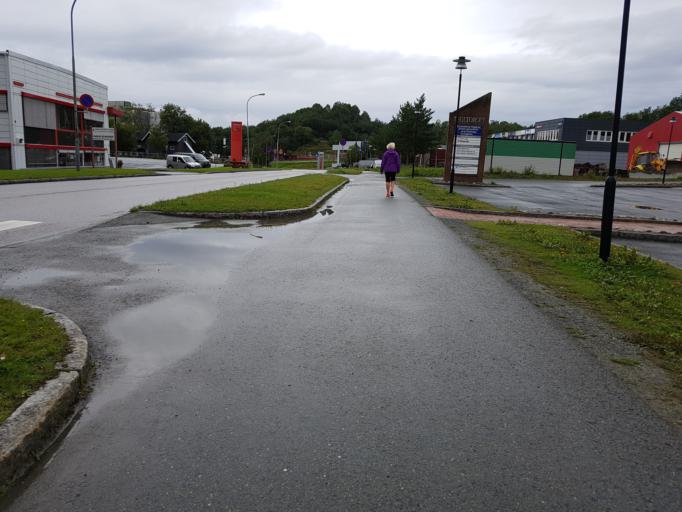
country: NO
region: Sor-Trondelag
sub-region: Trondheim
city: Trondheim
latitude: 63.3916
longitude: 10.4034
